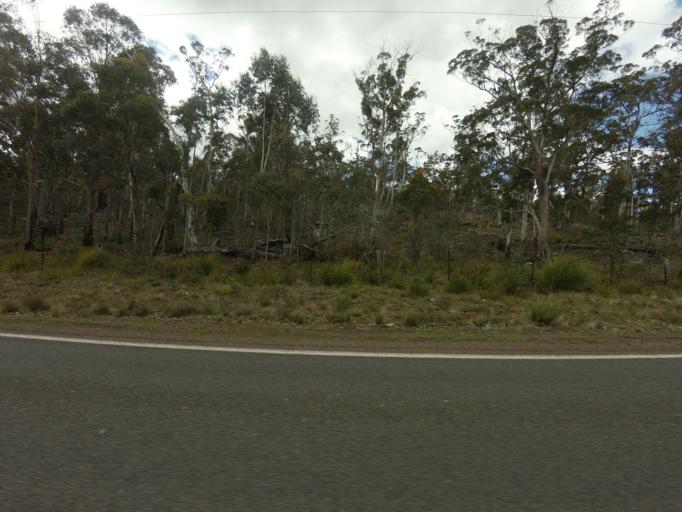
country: AU
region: Tasmania
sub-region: Northern Midlands
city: Evandale
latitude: -41.9936
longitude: 147.7140
